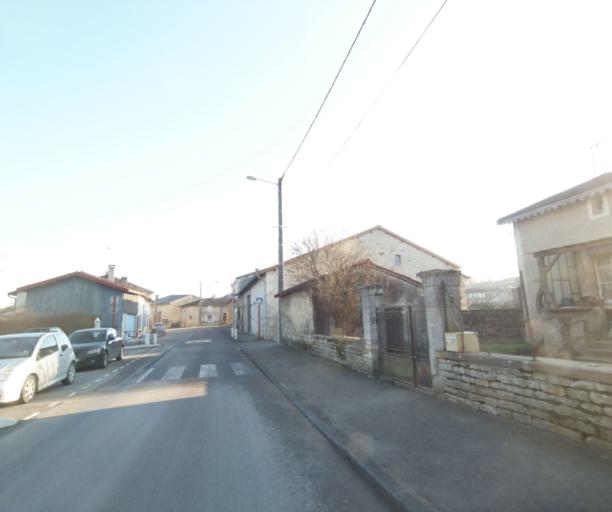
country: FR
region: Champagne-Ardenne
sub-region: Departement de la Haute-Marne
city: Bienville
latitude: 48.5622
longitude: 5.0507
